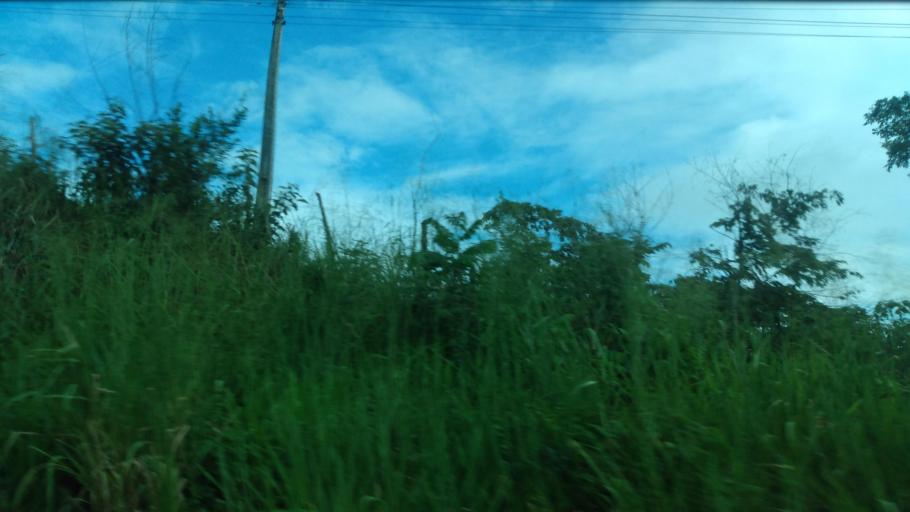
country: BR
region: Pernambuco
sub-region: Catende
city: Catende
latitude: -8.6930
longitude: -35.7150
